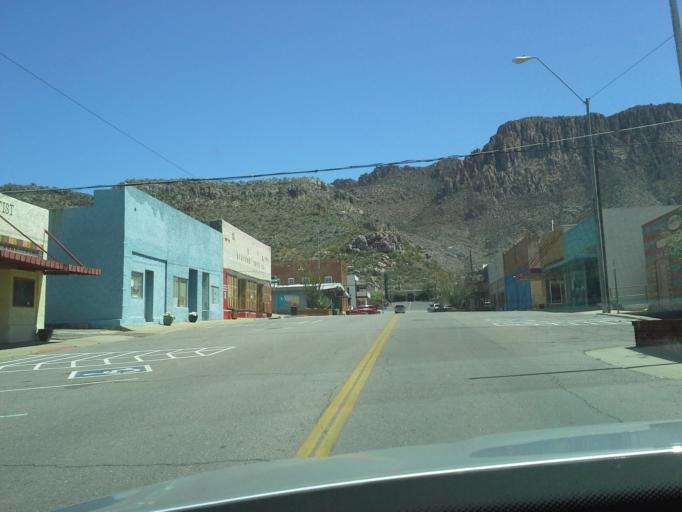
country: US
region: Arizona
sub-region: Pinal County
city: Superior
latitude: 33.2935
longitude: -111.0981
